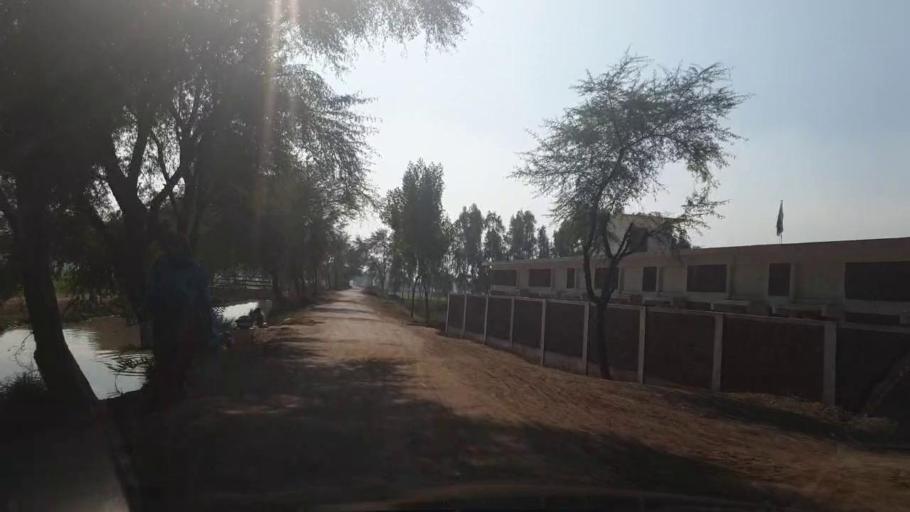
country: PK
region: Sindh
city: Khairpur
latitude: 28.1335
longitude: 69.6477
